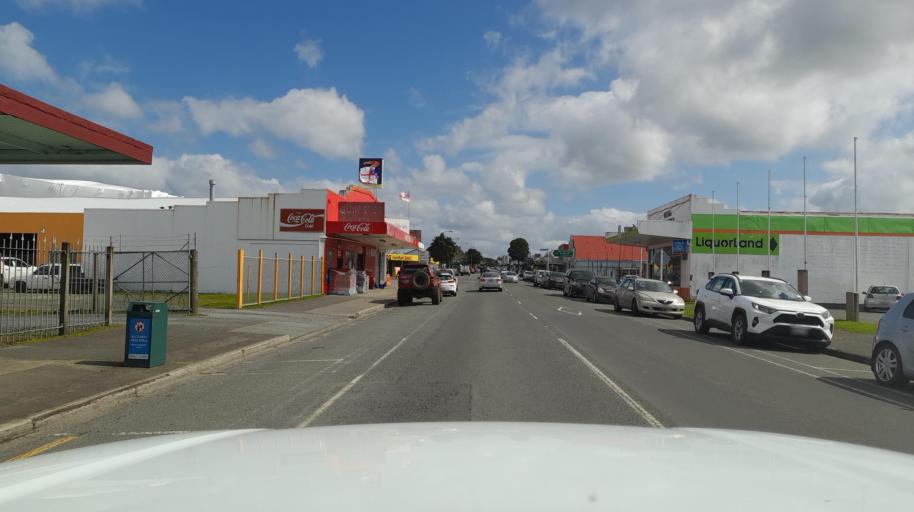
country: NZ
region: Northland
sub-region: Far North District
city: Waimate North
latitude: -35.4055
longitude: 173.8041
